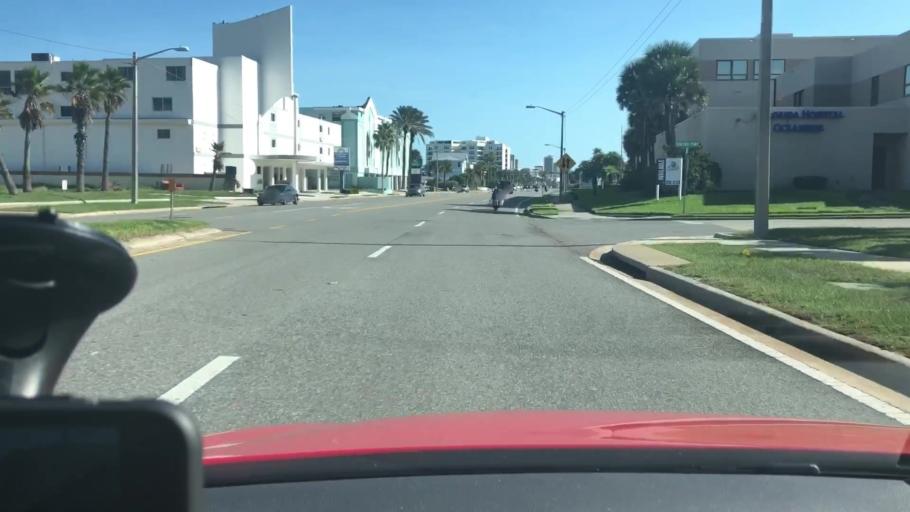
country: US
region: Florida
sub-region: Volusia County
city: Ormond Beach
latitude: 29.2854
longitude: -81.0369
